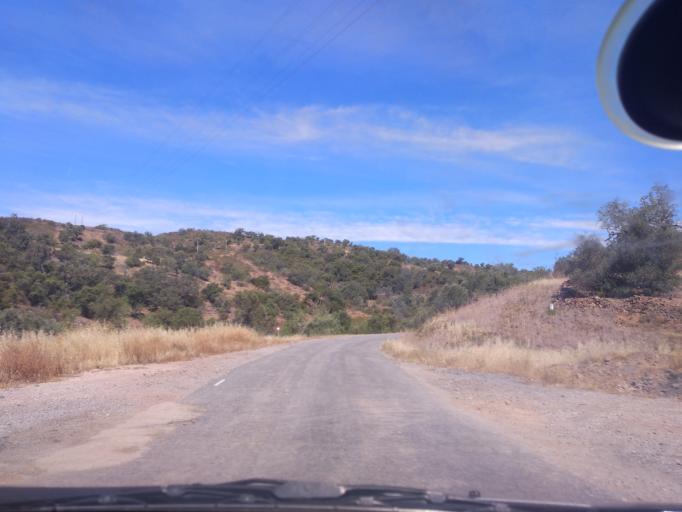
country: PT
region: Faro
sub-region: Olhao
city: Moncarapacho
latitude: 37.1553
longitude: -7.7967
